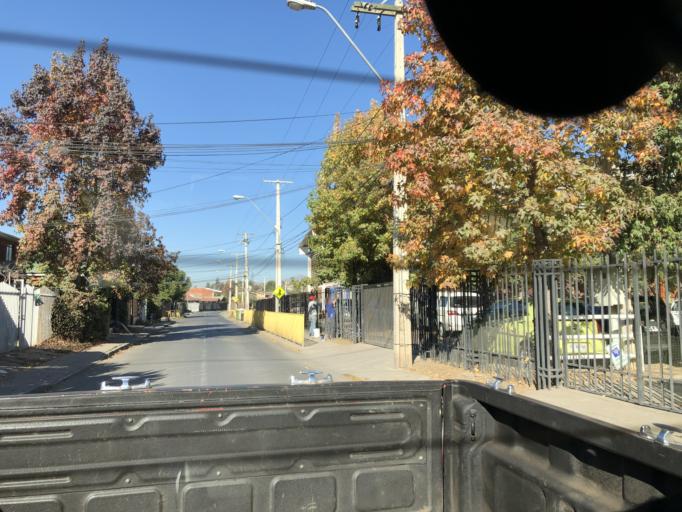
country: CL
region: Santiago Metropolitan
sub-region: Provincia de Cordillera
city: Puente Alto
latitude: -33.5926
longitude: -70.5577
